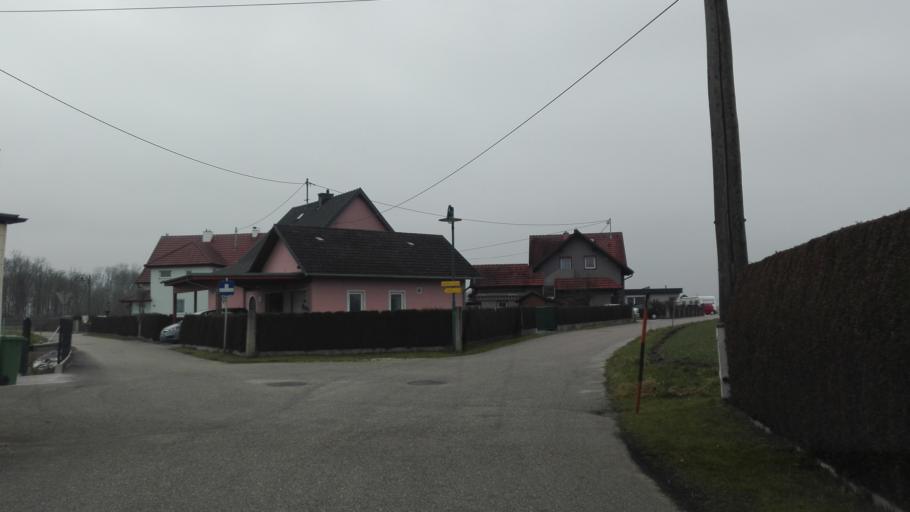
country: AT
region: Upper Austria
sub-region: Politischer Bezirk Linz-Land
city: Horsching
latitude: 48.2319
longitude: 14.1560
